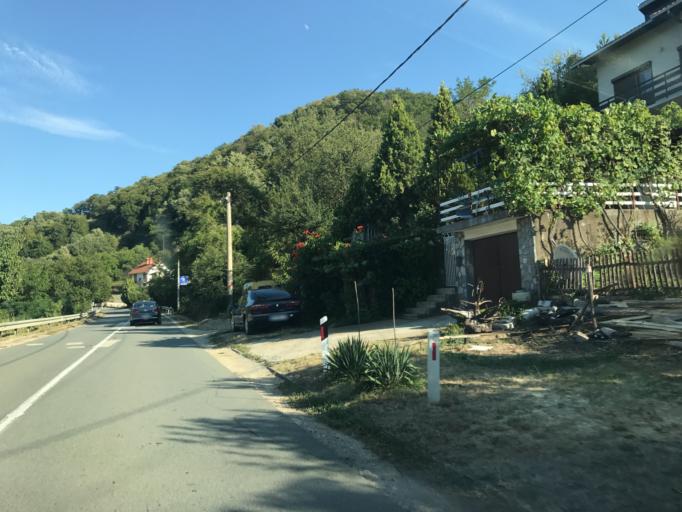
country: RO
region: Mehedinti
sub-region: Comuna Svinita
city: Svinita
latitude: 44.4659
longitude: 22.1307
